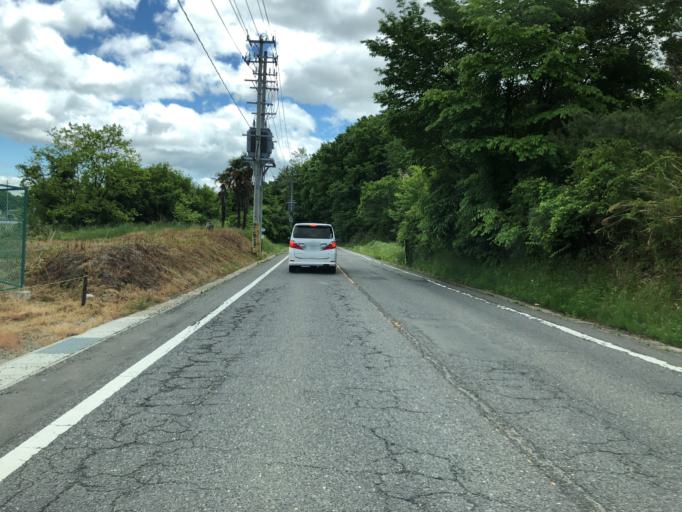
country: JP
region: Fukushima
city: Motomiya
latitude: 37.5122
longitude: 140.4216
